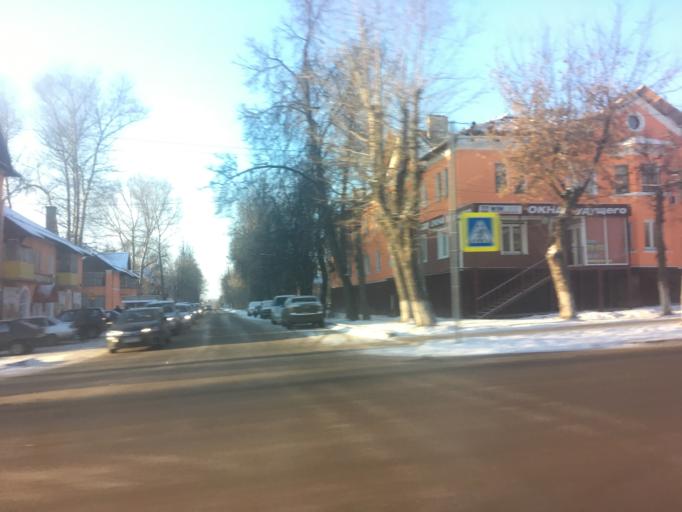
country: RU
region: Tula
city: Tula
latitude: 54.2071
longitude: 37.6741
